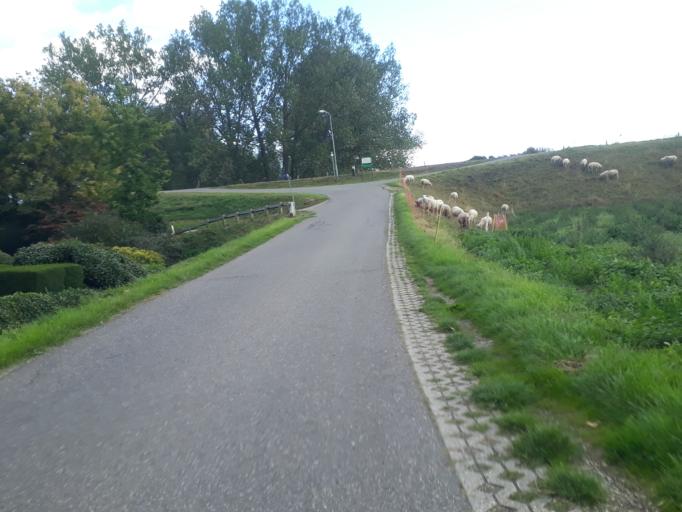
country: NL
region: Gelderland
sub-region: Gemeente Zevenaar
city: Zevenaar
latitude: 51.9153
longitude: 6.0709
